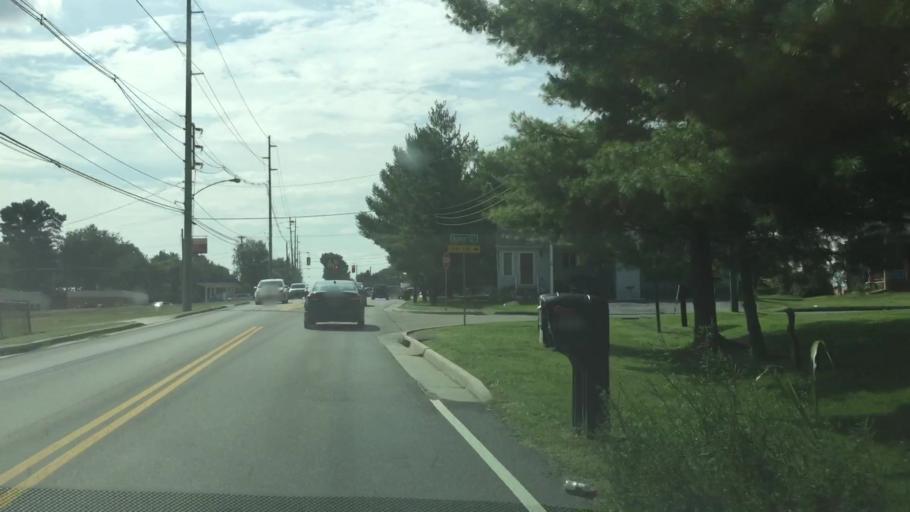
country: US
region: Tennessee
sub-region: Sullivan County
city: Fairmount
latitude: 36.6096
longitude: -82.1375
